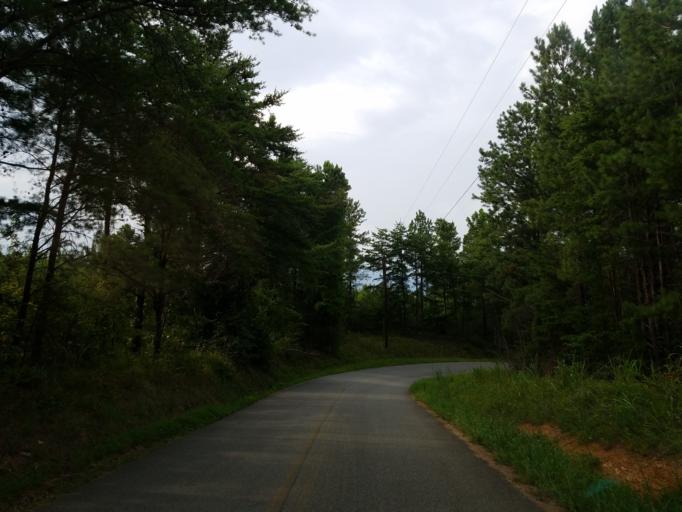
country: US
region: Georgia
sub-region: Bartow County
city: Rydal
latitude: 34.3803
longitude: -84.6827
